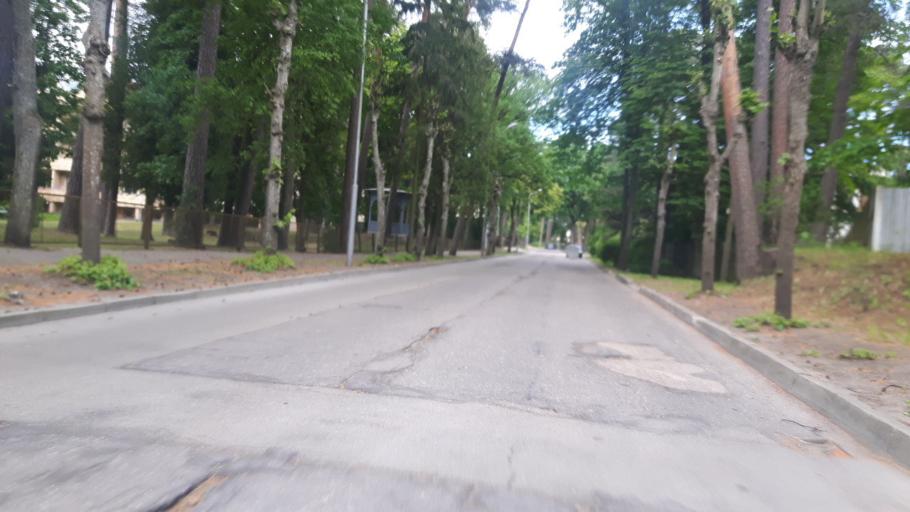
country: LV
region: Jurmala
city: Jurmala
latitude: 56.9780
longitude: 23.8262
